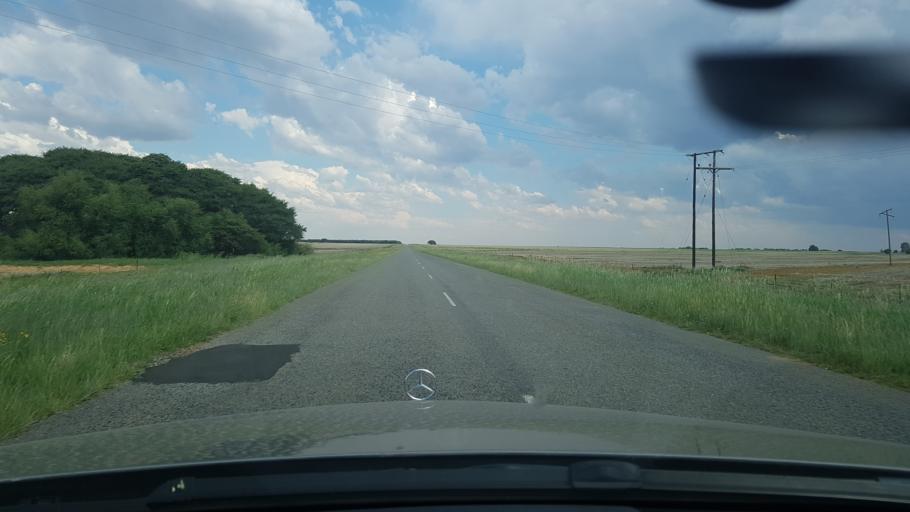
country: ZA
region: North-West
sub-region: Dr Ruth Segomotsi Mompati District Municipality
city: Bloemhof
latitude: -27.8564
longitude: 25.6505
